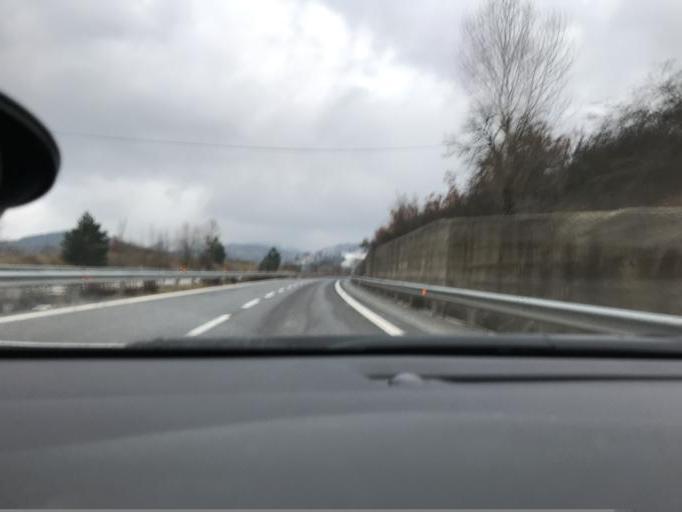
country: IT
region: The Marches
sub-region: Provincia di Ancona
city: Fabriano
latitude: 43.3289
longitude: 12.9245
